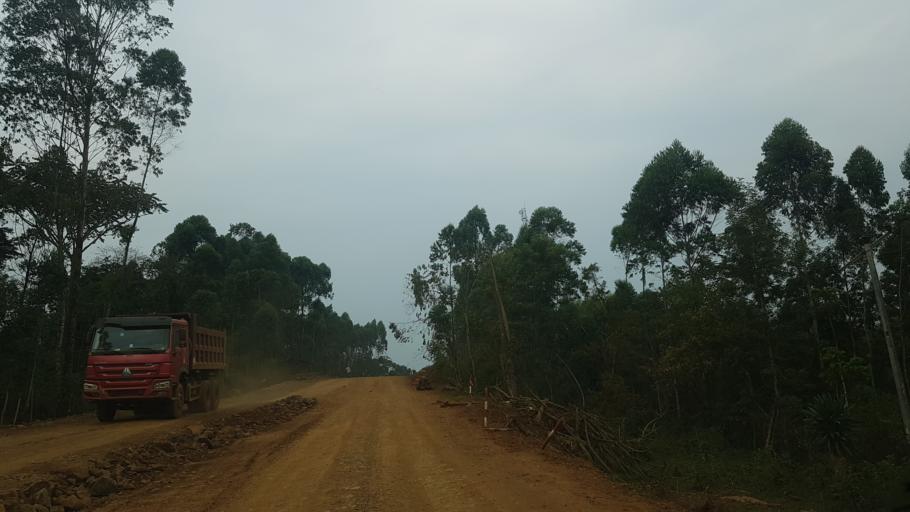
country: ET
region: Oromiya
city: Gore
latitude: 7.9010
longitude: 35.4985
